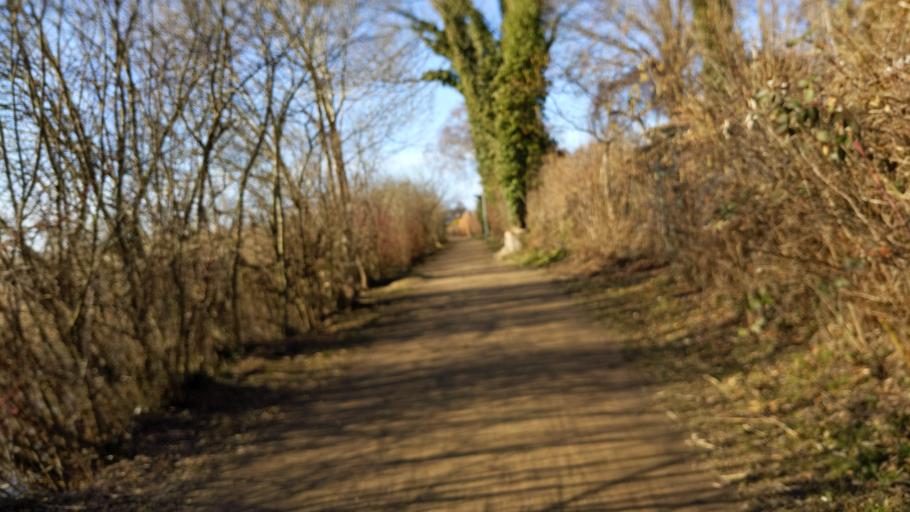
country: DE
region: Schleswig-Holstein
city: Susel
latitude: 54.0338
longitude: 10.7006
